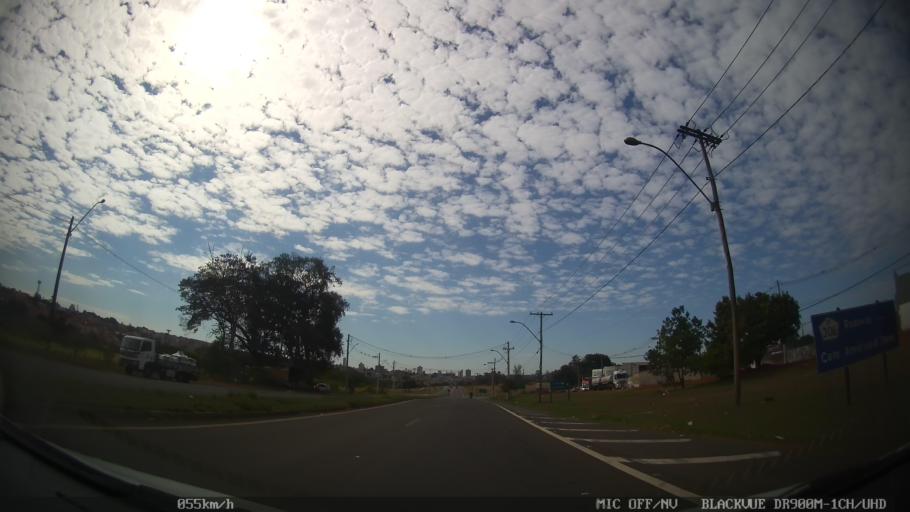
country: BR
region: Sao Paulo
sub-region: Santa Barbara D'Oeste
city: Santa Barbara d'Oeste
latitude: -22.7691
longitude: -47.4210
